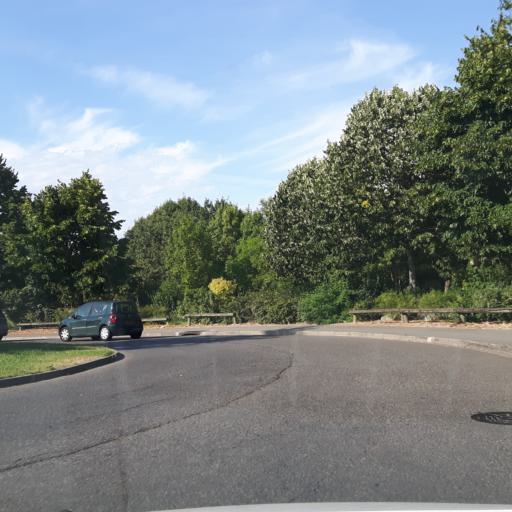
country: FR
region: Midi-Pyrenees
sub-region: Departement de la Haute-Garonne
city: Balma
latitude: 43.5903
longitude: 1.4908
